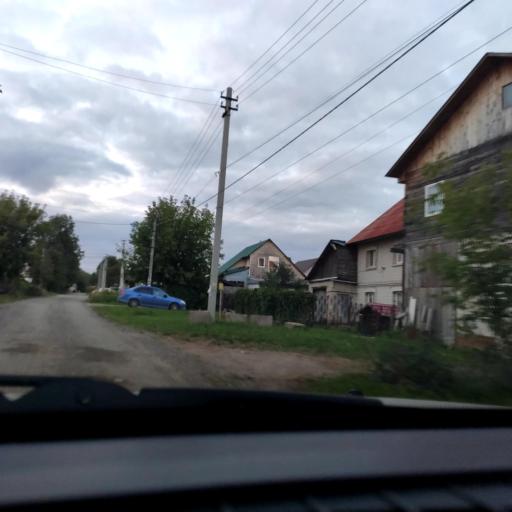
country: RU
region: Perm
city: Perm
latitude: 58.0458
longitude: 56.3326
